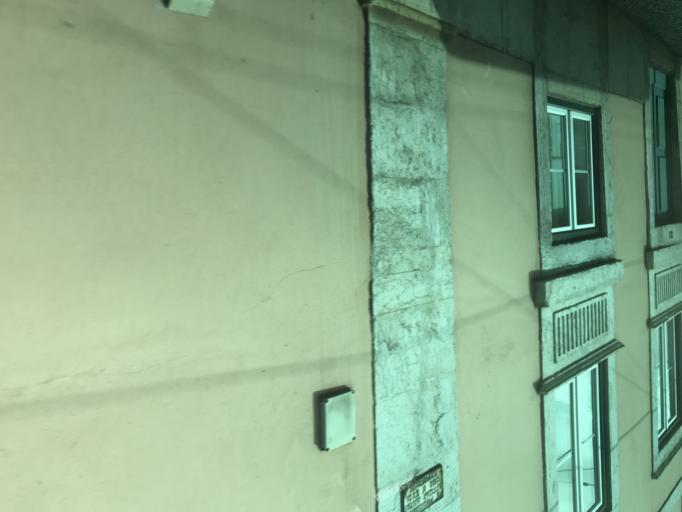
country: PT
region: Setubal
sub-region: Almada
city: Pragal
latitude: 38.7018
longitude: -9.1812
